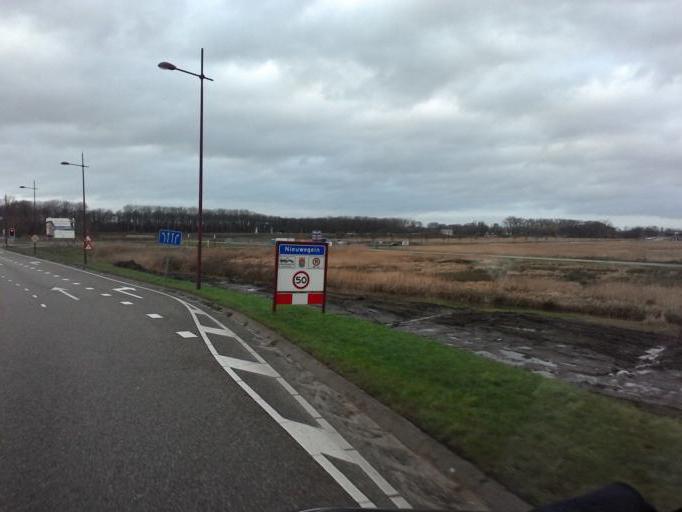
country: NL
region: Utrecht
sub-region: Gemeente Vianen
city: Vianen
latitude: 52.0137
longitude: 5.1169
